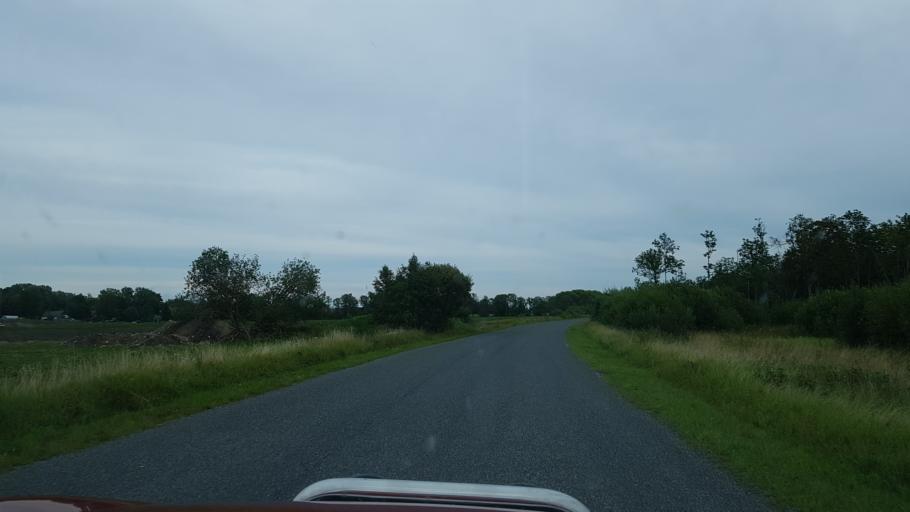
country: EE
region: Laeaene
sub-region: Lihula vald
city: Lihula
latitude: 58.8833
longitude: 23.8378
